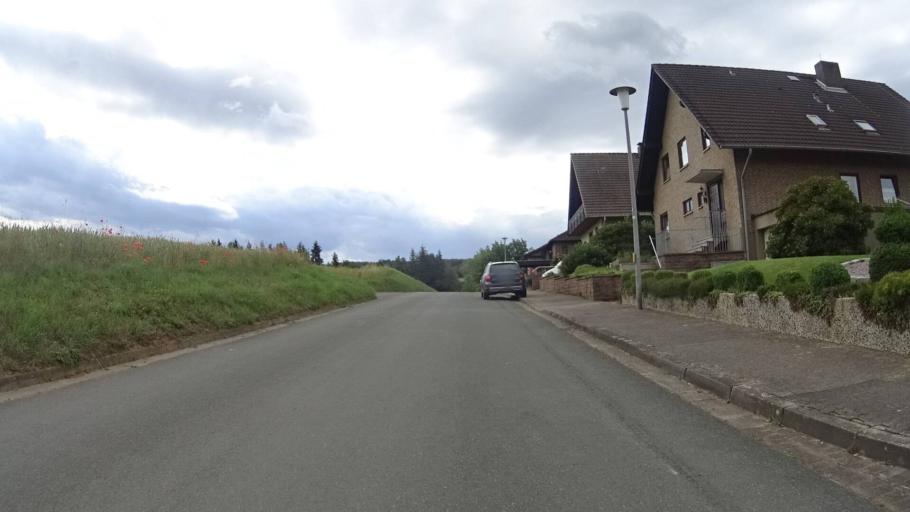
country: DE
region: Lower Saxony
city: Bevern
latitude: 51.8592
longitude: 9.5069
